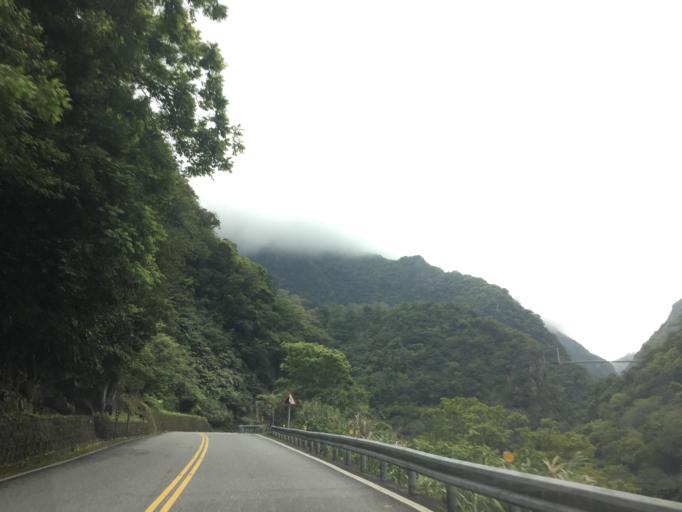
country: TW
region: Taiwan
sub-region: Hualien
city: Hualian
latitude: 24.1743
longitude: 121.5800
